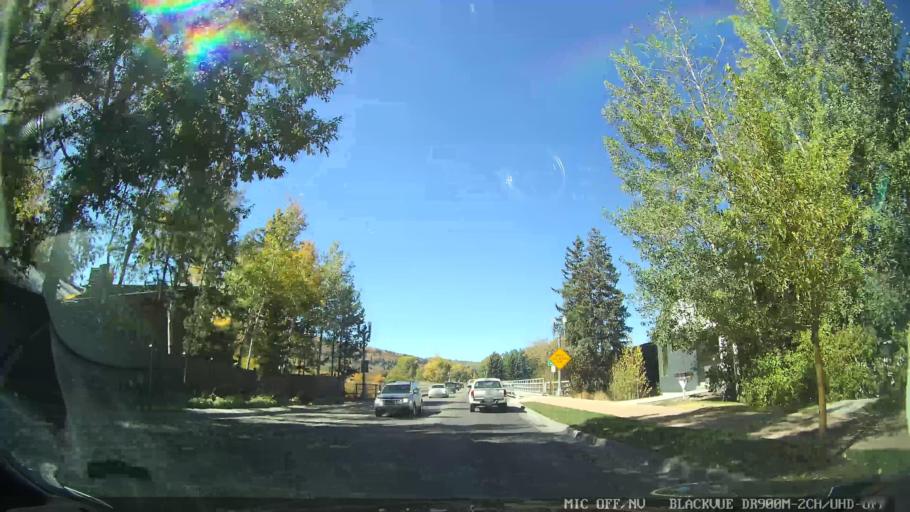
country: US
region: Colorado
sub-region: Pitkin County
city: Aspen
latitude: 39.1950
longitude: -106.8320
